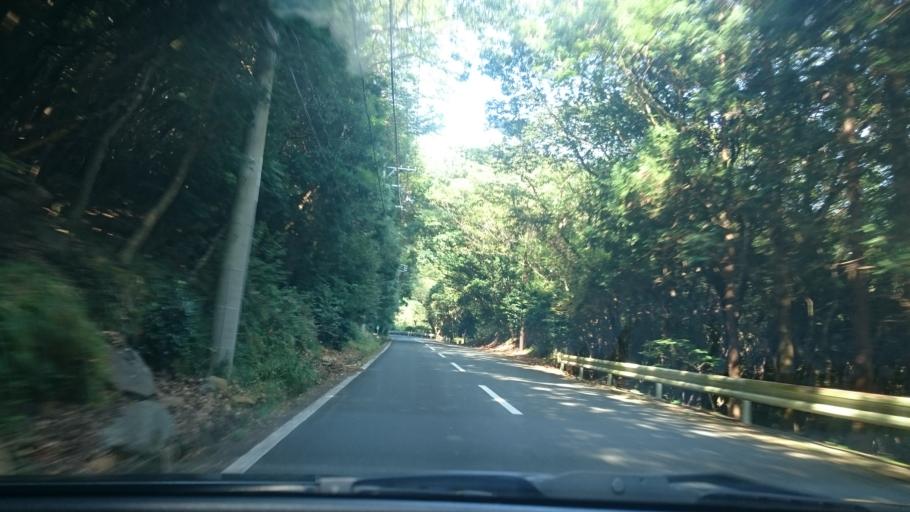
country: JP
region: Shizuoka
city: Heda
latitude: 34.9507
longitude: 138.7752
